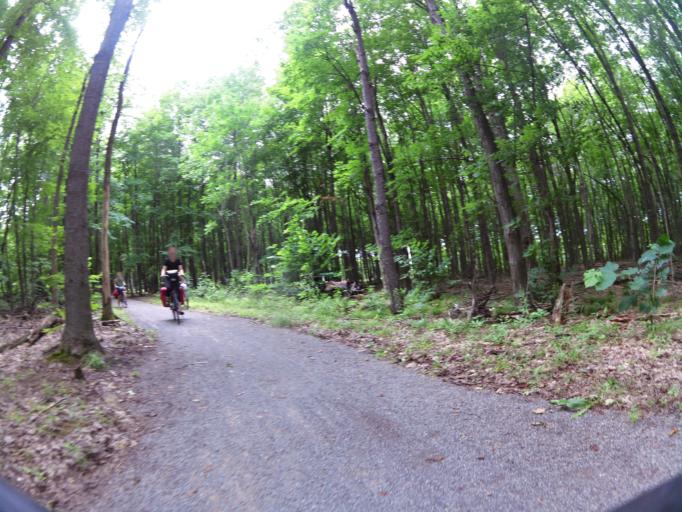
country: CA
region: Ontario
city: Bells Corners
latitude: 45.0290
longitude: -75.6747
